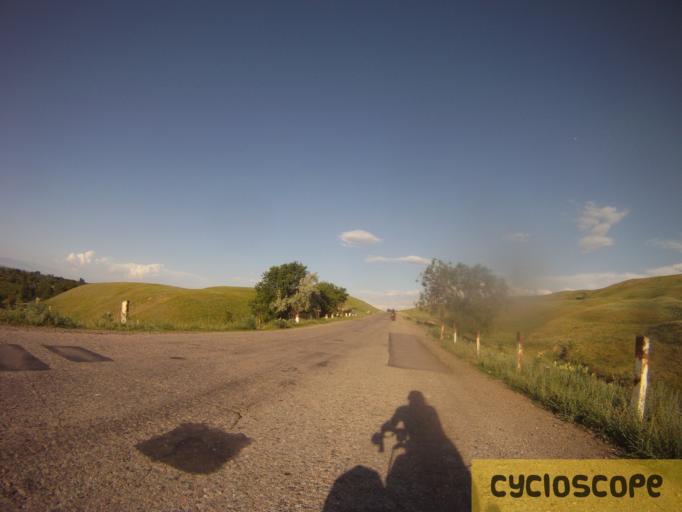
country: KZ
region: Almaty Oblysy
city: Turgen'
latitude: 43.4836
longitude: 77.7674
